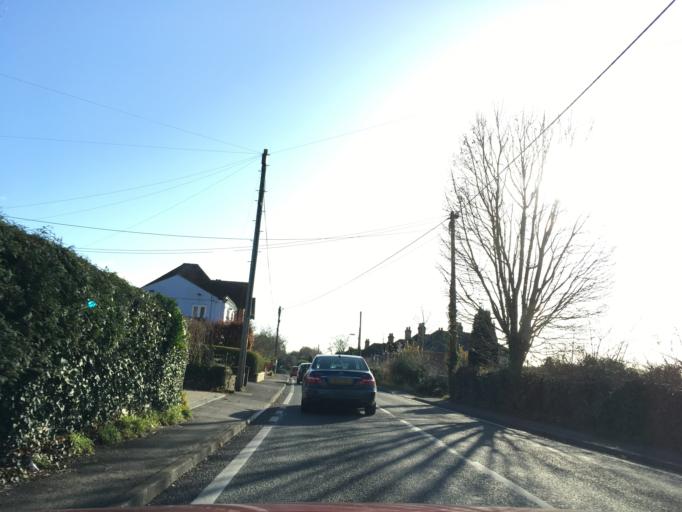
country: GB
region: England
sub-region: Hampshire
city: Colden Common
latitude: 51.0008
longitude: -1.3169
